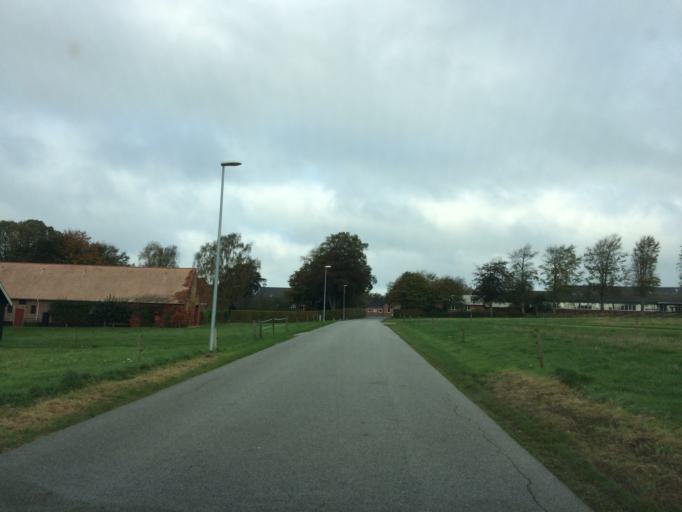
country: DK
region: Central Jutland
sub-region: Holstebro Kommune
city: Holstebro
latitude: 56.3367
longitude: 8.4860
